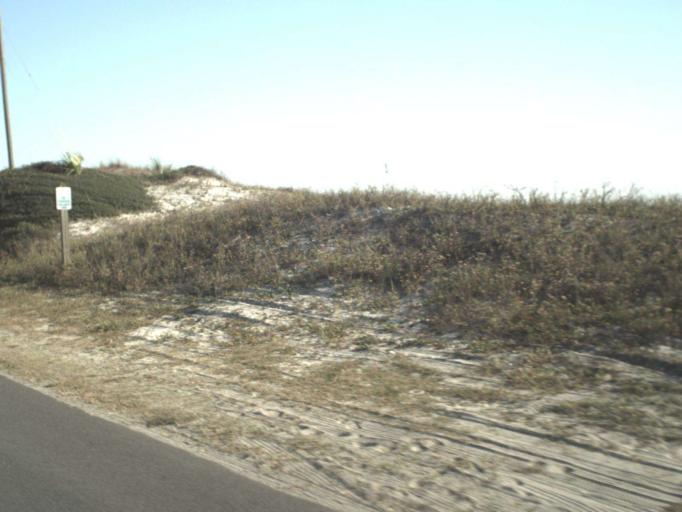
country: US
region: Florida
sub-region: Bay County
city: Laguna Beach
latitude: 30.2481
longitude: -85.9434
